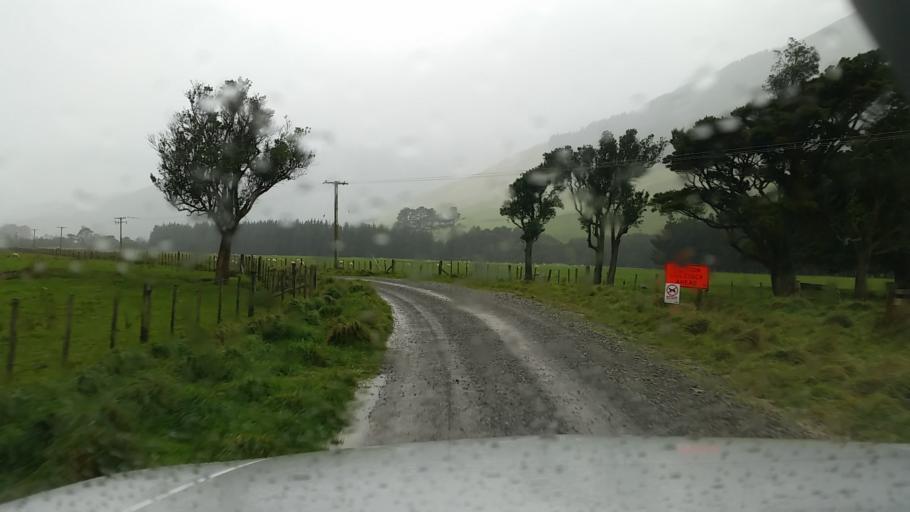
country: NZ
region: Marlborough
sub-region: Marlborough District
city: Picton
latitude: -41.1280
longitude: 174.0402
